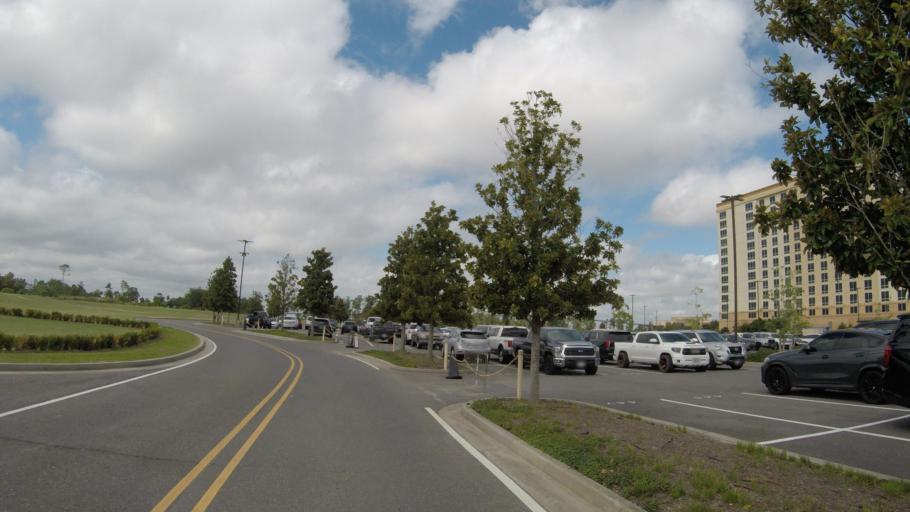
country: US
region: Louisiana
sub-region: Calcasieu Parish
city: Prien
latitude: 30.2029
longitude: -93.2633
